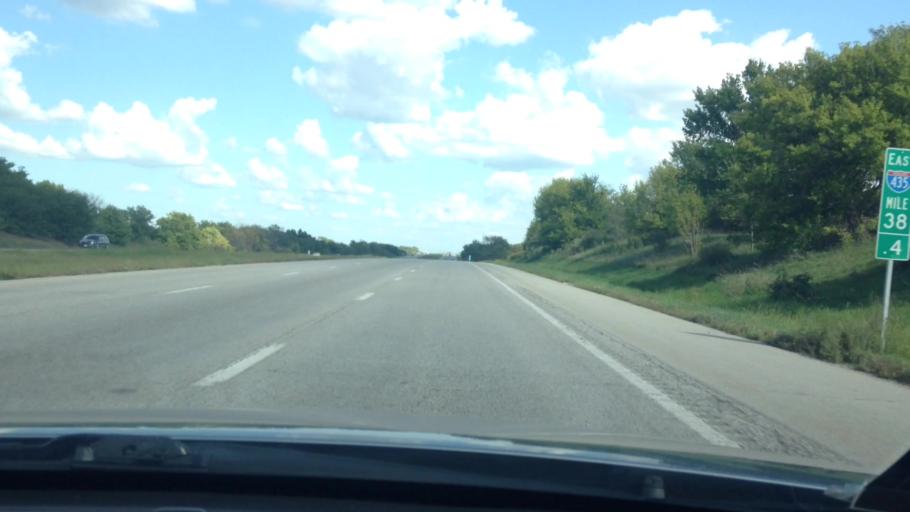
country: US
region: Missouri
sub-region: Platte County
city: Weatherby Lake
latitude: 39.3073
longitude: -94.6366
